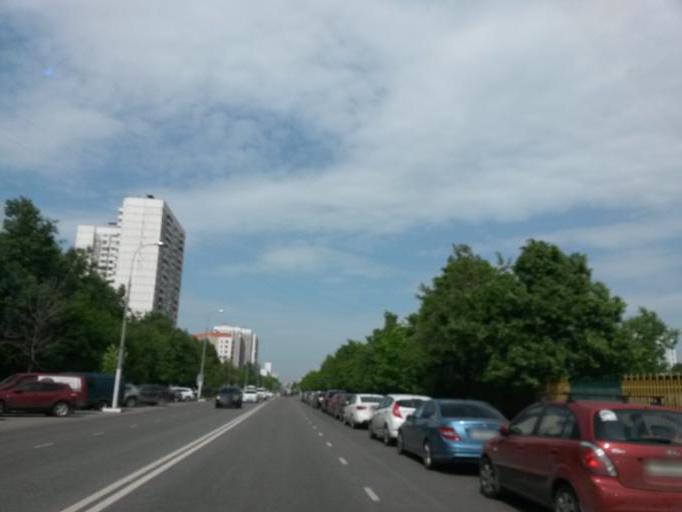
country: RU
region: Moscow
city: Chertanovo Yuzhnoye
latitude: 55.6016
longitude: 37.5989
